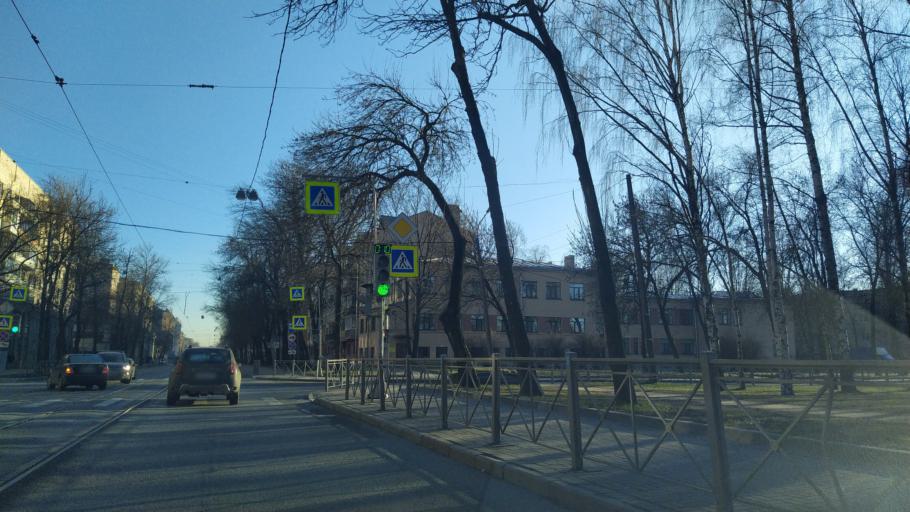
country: RU
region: Leningrad
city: Sampsonievskiy
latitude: 59.9908
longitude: 30.3326
